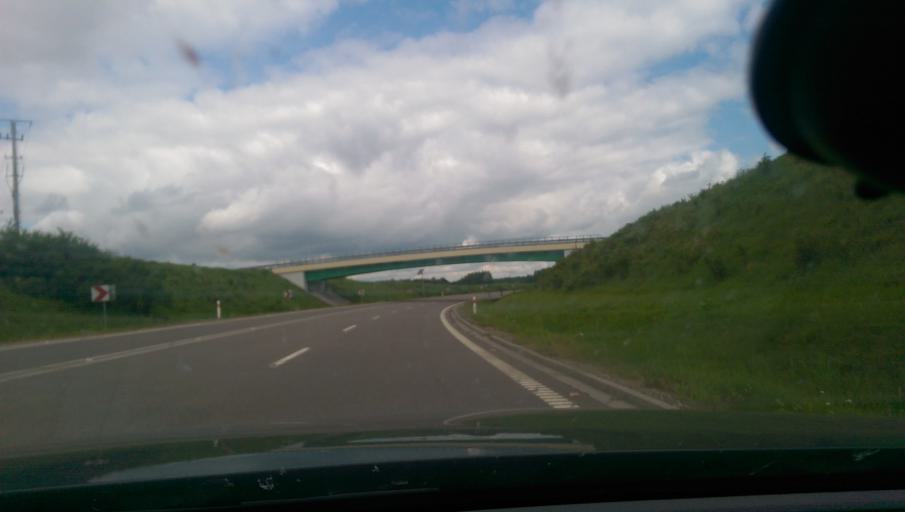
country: PL
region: Warmian-Masurian Voivodeship
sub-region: Powiat goldapski
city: Goldap
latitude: 54.2992
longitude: 22.2817
